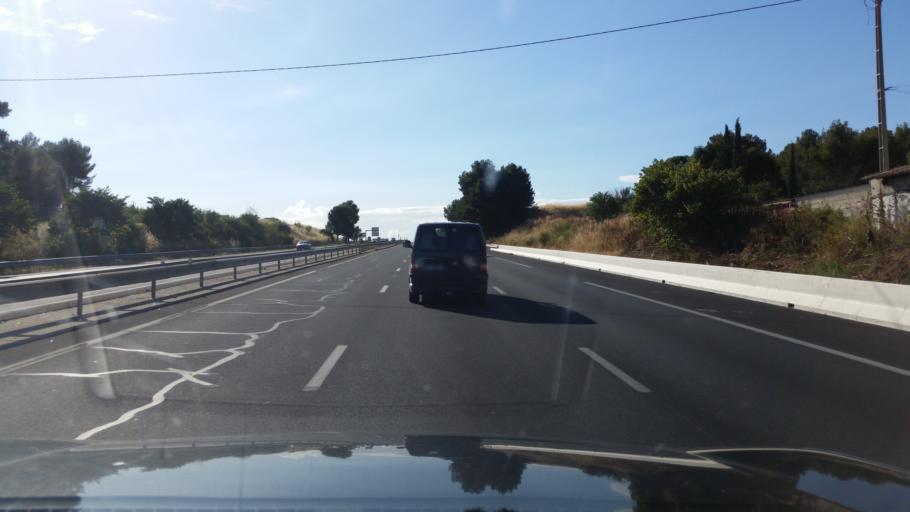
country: FR
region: Provence-Alpes-Cote d'Azur
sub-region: Departement des Bouches-du-Rhone
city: Aix-en-Provence
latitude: 43.5247
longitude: 5.4064
